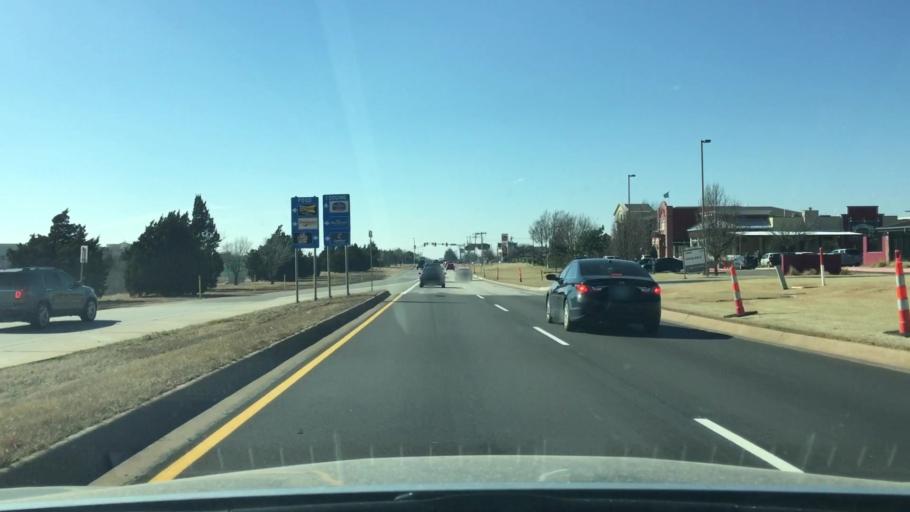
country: US
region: Oklahoma
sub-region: Oklahoma County
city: The Village
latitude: 35.6098
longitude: -97.5637
